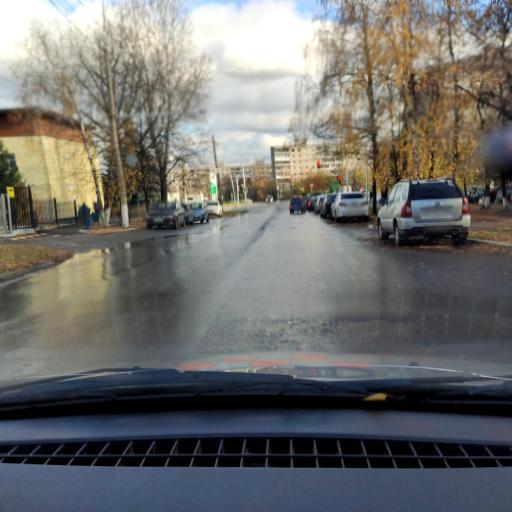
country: RU
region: Bashkortostan
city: Ufa
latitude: 54.7814
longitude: 56.0360
